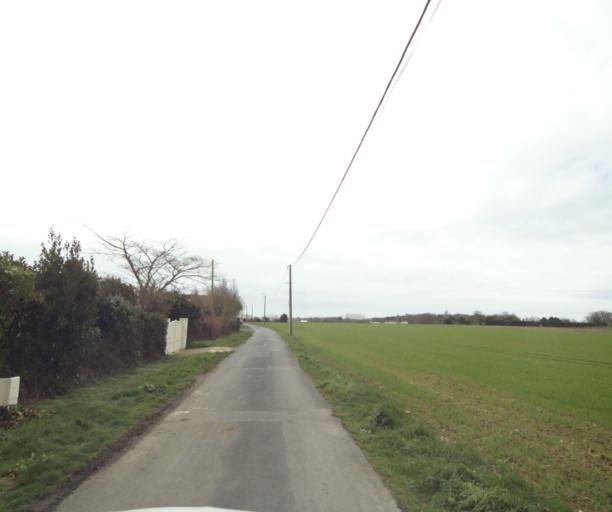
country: FR
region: Poitou-Charentes
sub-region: Departement de la Charente-Maritime
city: Lagord
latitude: 46.1870
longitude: -1.1682
